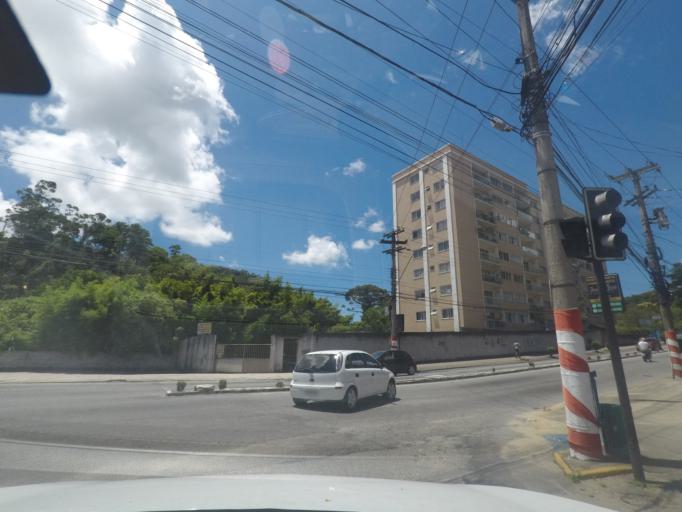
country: BR
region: Rio de Janeiro
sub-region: Teresopolis
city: Teresopolis
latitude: -22.4232
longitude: -42.9777
